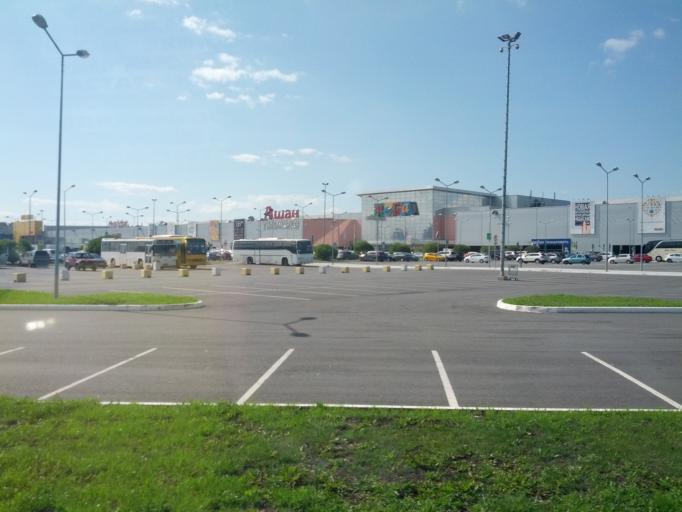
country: RU
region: Leningrad
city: Rybatskoye
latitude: 59.8920
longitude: 30.5193
